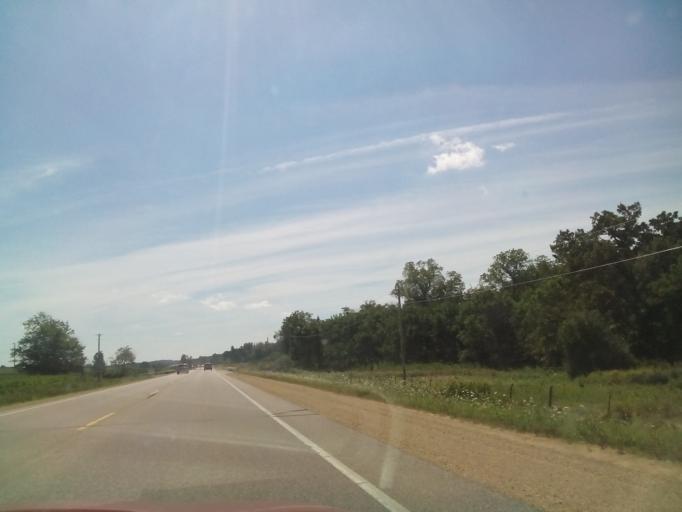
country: US
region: Wisconsin
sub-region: Green County
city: Monticello
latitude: 42.7620
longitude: -89.6172
